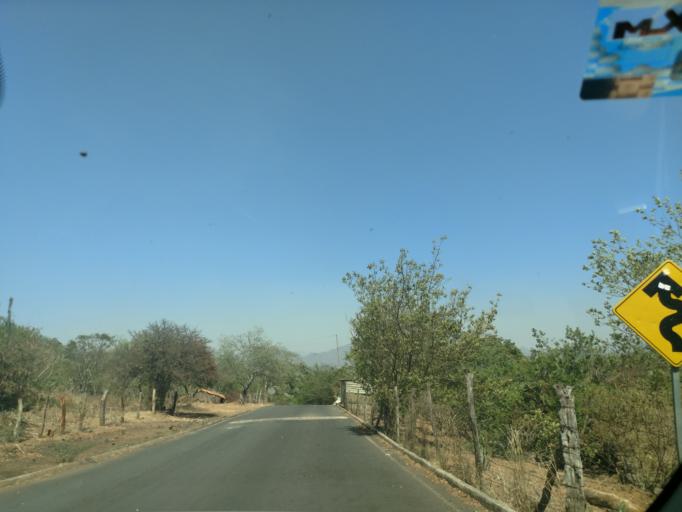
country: MX
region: Nayarit
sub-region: Tepic
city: La Corregidora
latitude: 21.4702
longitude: -104.6623
